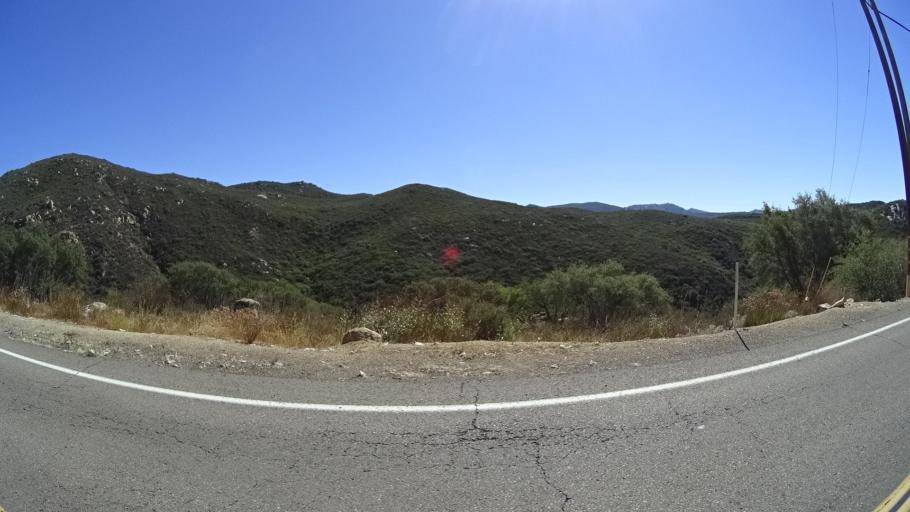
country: US
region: California
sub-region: San Diego County
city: Descanso
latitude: 32.8078
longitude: -116.6361
